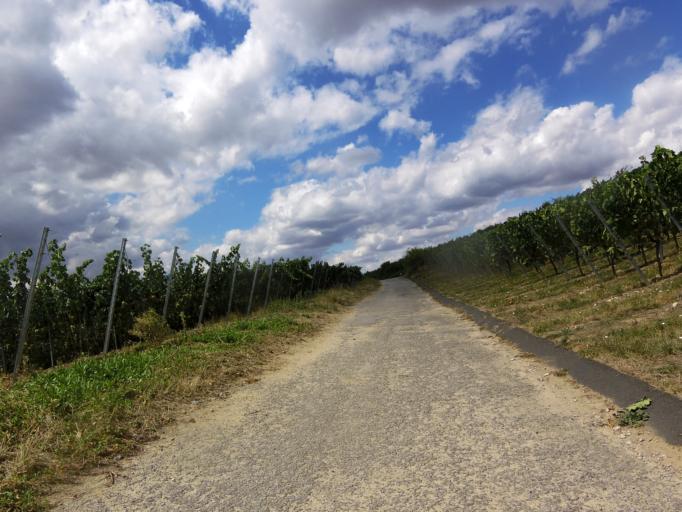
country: DE
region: Bavaria
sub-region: Regierungsbezirk Unterfranken
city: Winterhausen
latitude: 49.7234
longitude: 10.0162
